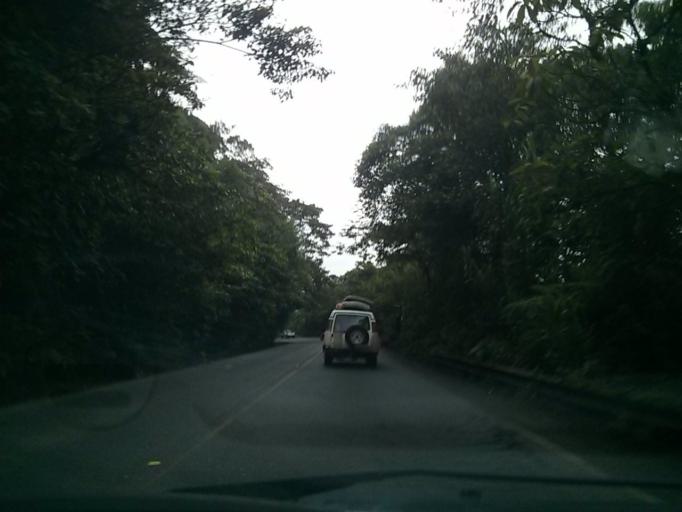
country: CR
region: San Jose
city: Dulce Nombre de Jesus
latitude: 10.1229
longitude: -83.9714
